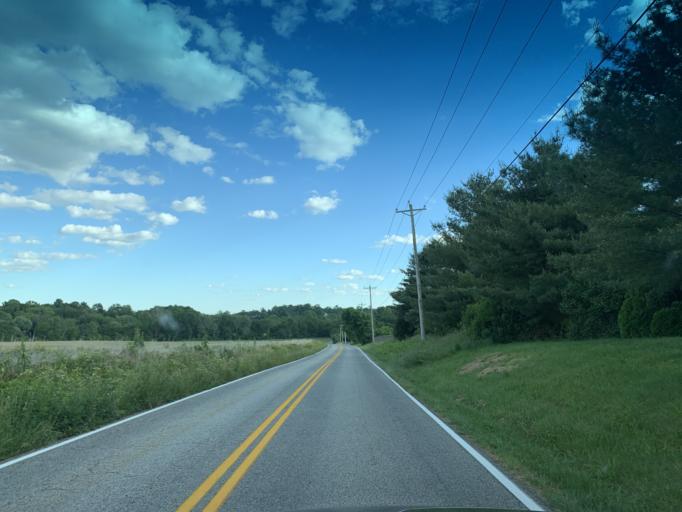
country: US
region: Maryland
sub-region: Cecil County
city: Rising Sun
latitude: 39.6445
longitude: -76.0413
